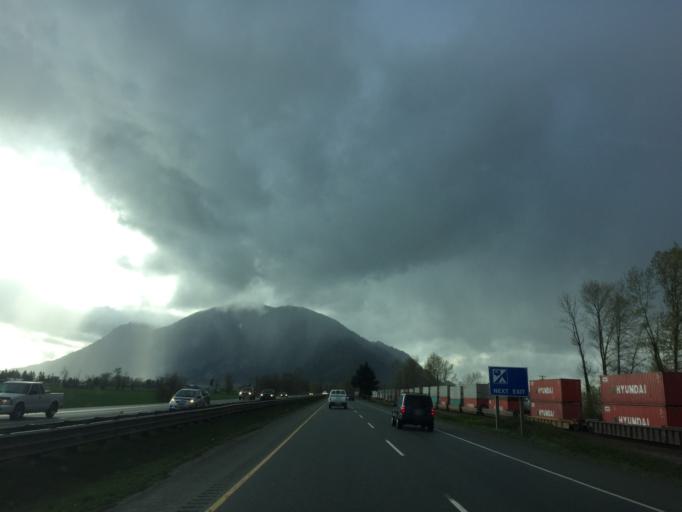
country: CA
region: British Columbia
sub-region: Fraser Valley Regional District
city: Chilliwack
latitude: 49.1401
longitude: -122.0477
